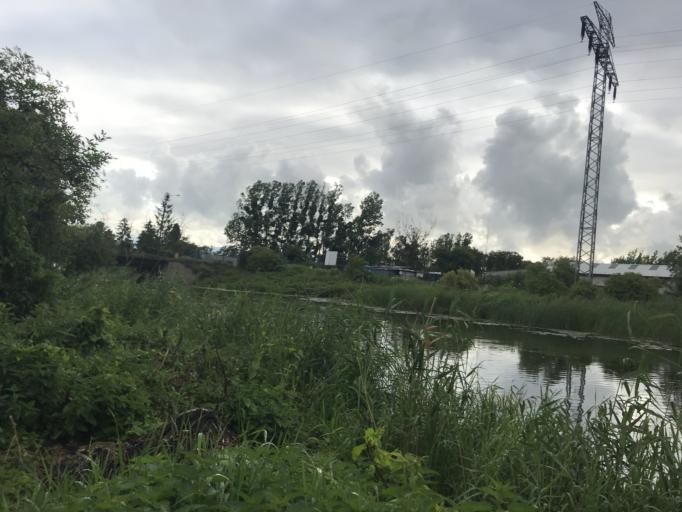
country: PL
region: Pomeranian Voivodeship
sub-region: Gdansk
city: Gdansk
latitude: 54.3508
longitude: 18.6758
